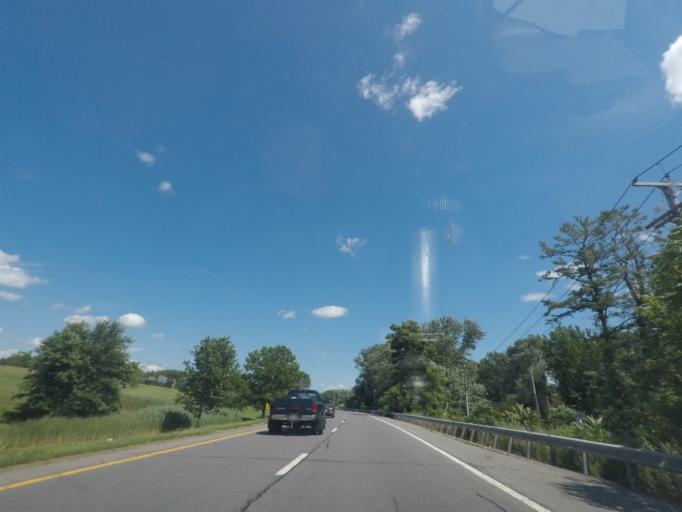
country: US
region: New York
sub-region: Schenectady County
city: Scotia
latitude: 42.8136
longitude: -73.9790
